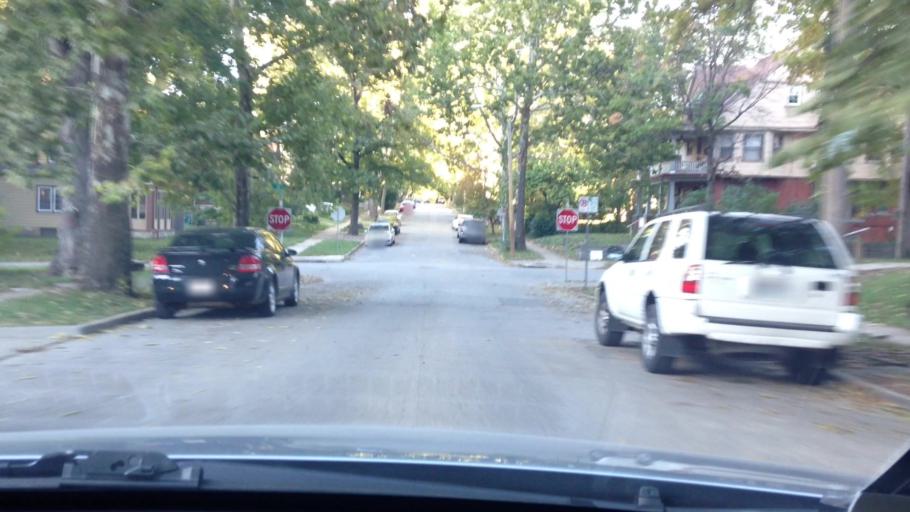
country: US
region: Kansas
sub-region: Johnson County
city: Westwood
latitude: 39.0585
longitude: -94.6061
